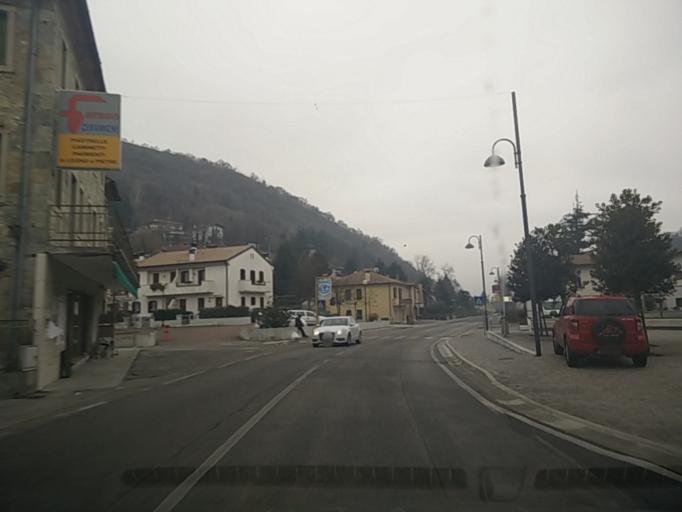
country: IT
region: Veneto
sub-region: Provincia di Treviso
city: Tarzo
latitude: 45.9789
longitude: 12.2306
